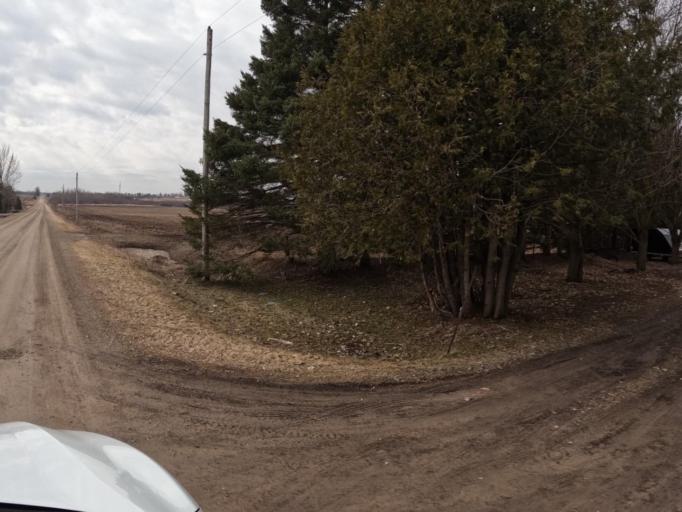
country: CA
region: Ontario
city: Orangeville
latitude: 43.9397
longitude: -80.1901
